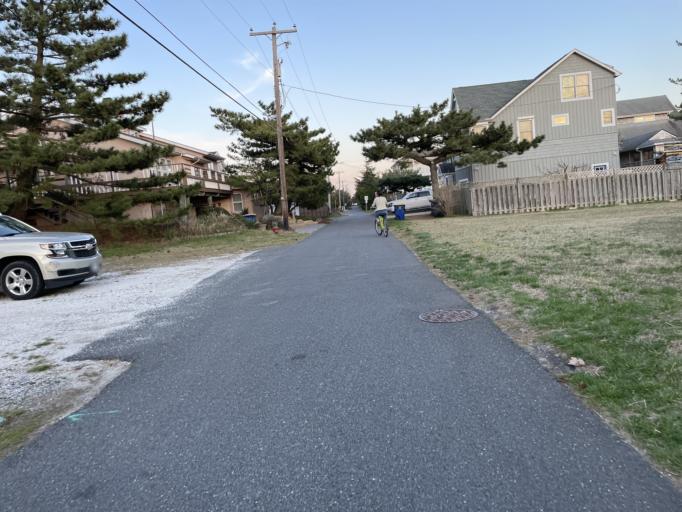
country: US
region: Delaware
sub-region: Sussex County
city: Lewes
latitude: 38.7883
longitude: -75.1564
